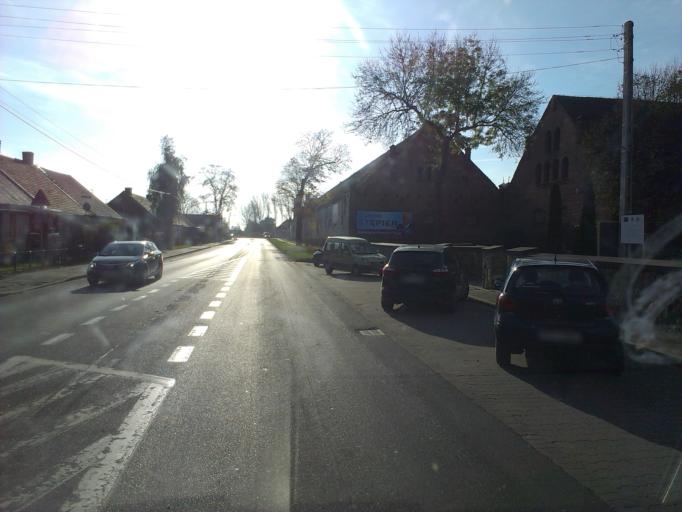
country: PL
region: West Pomeranian Voivodeship
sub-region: Powiat pyrzycki
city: Pyrzyce
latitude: 53.1861
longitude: 14.8397
